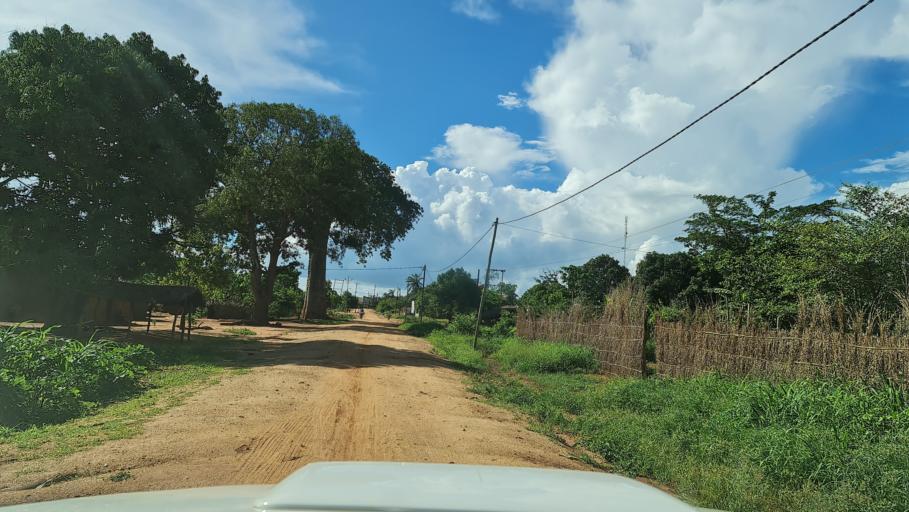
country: MZ
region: Nampula
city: Ilha de Mocambique
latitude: -15.2911
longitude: 40.1168
